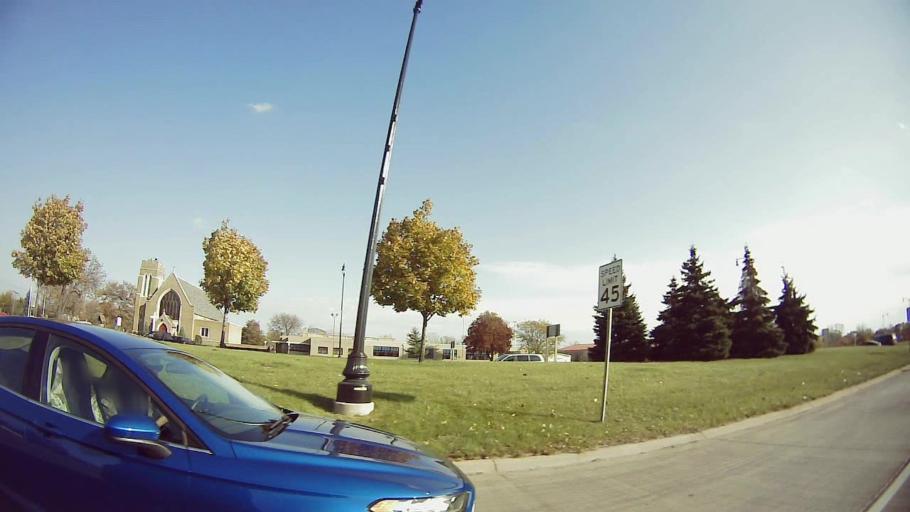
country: US
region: Michigan
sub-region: Wayne County
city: Taylor
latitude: 42.2109
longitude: -83.2689
